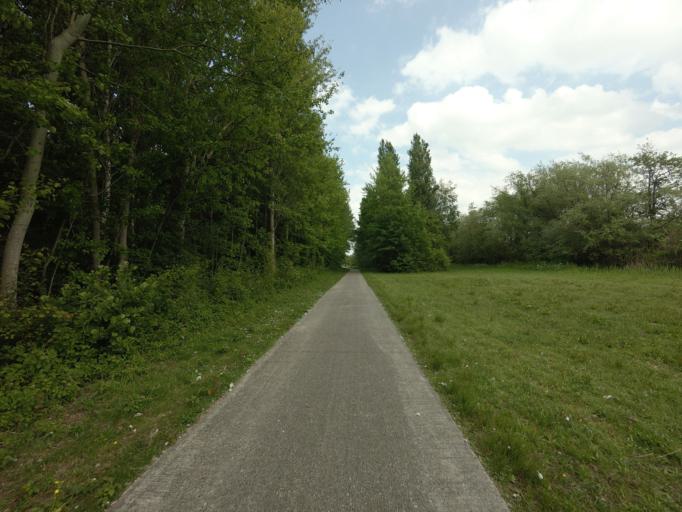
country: NL
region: Zeeland
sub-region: Schouwen-Duiveland
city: Bruinisse
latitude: 51.6743
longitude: 4.1059
